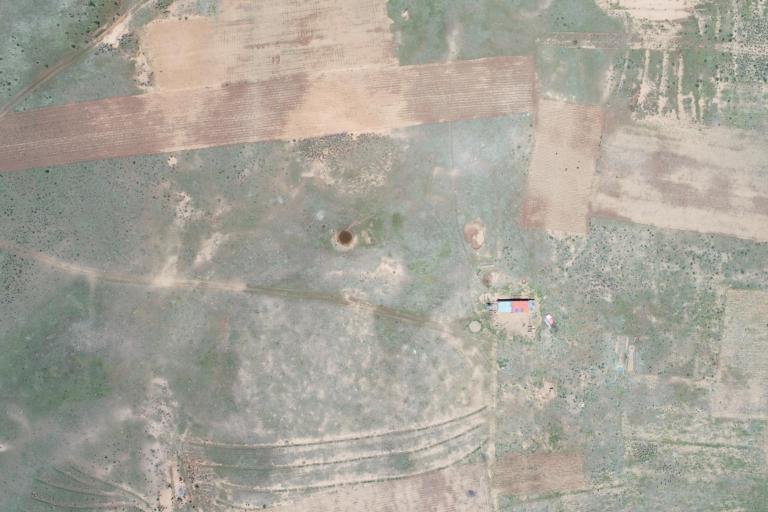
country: BO
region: La Paz
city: Patacamaya
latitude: -17.2736
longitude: -68.5110
